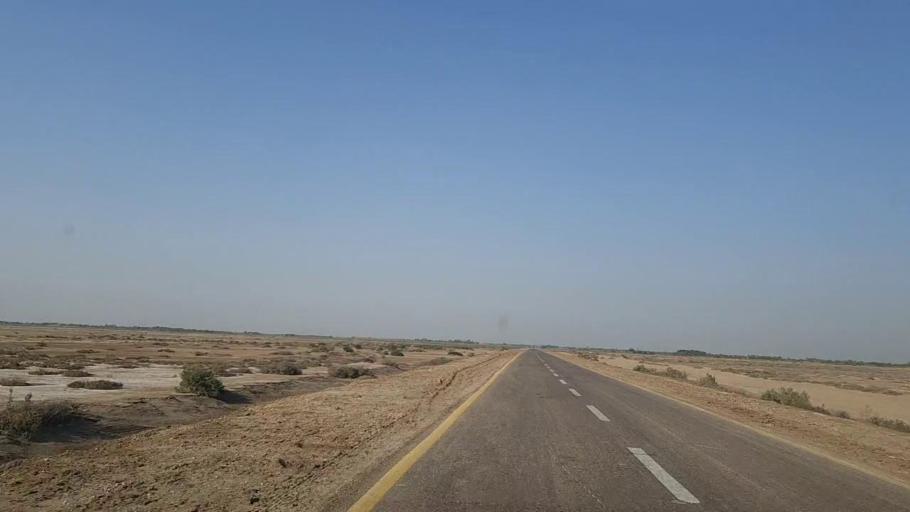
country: PK
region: Sindh
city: Jati
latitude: 24.4980
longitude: 68.3768
